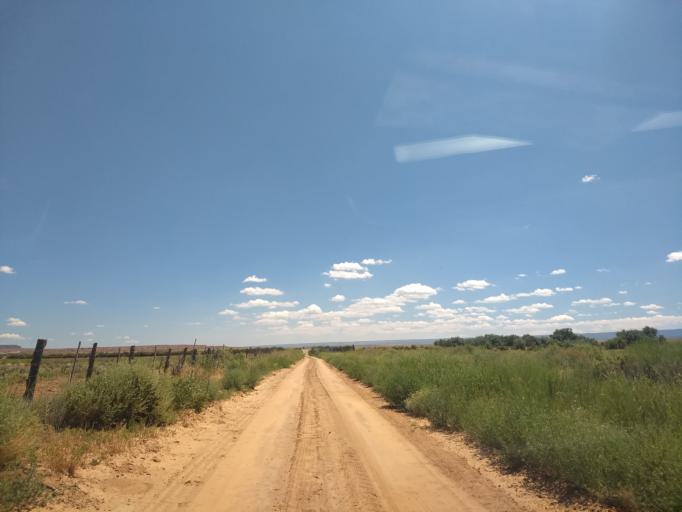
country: US
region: Arizona
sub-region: Coconino County
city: Fredonia
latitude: 36.9251
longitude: -112.5423
